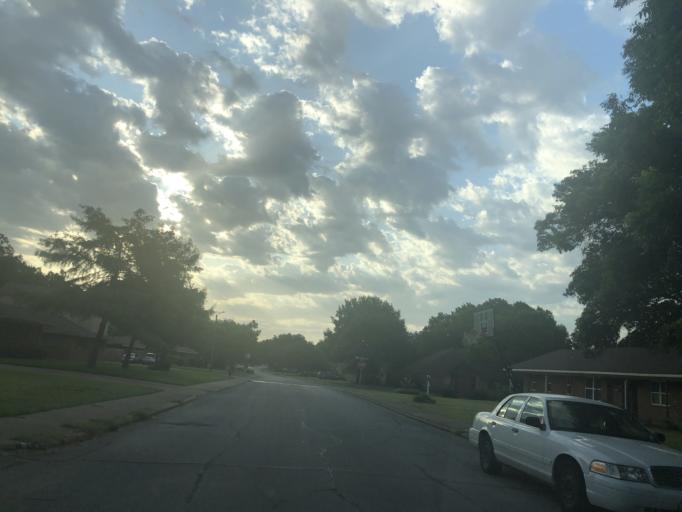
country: US
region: Texas
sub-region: Dallas County
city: Grand Prairie
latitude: 32.7633
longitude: -97.0179
